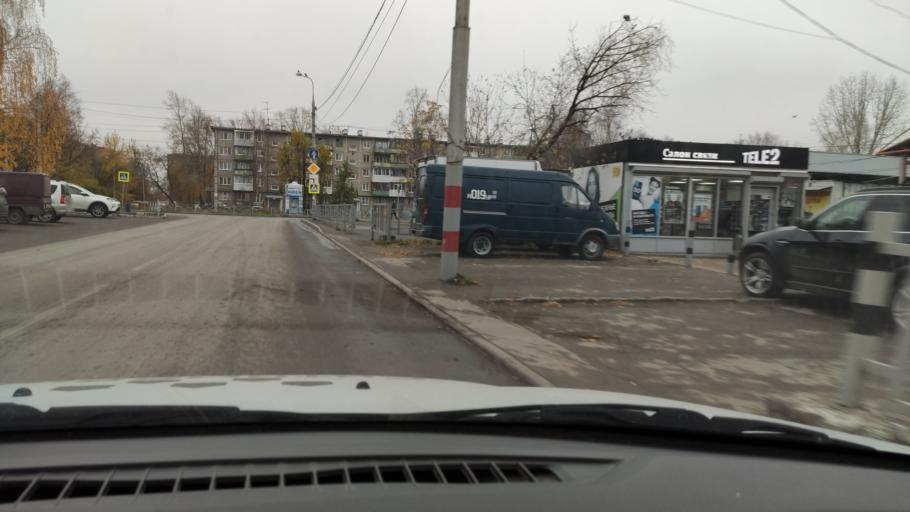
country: RU
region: Perm
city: Perm
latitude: 57.9651
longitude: 56.2192
